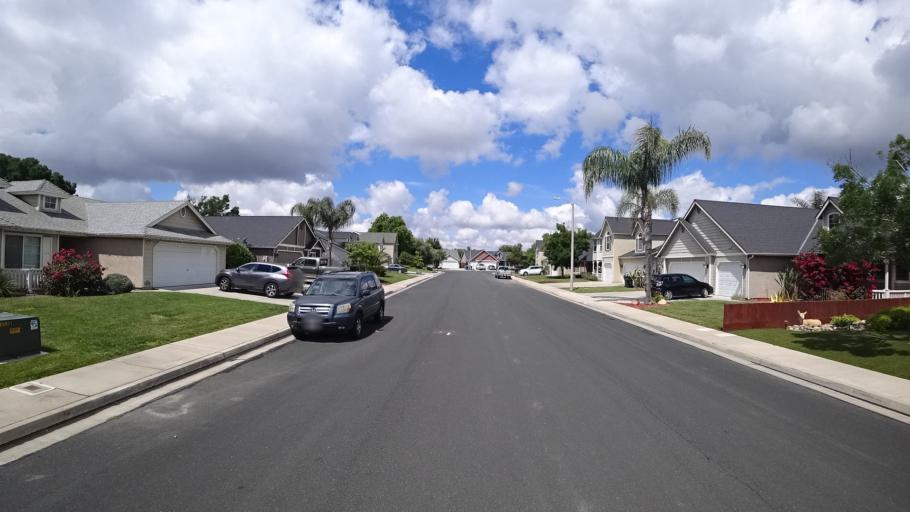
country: US
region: California
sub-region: Kings County
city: Lucerne
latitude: 36.3649
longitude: -119.6588
